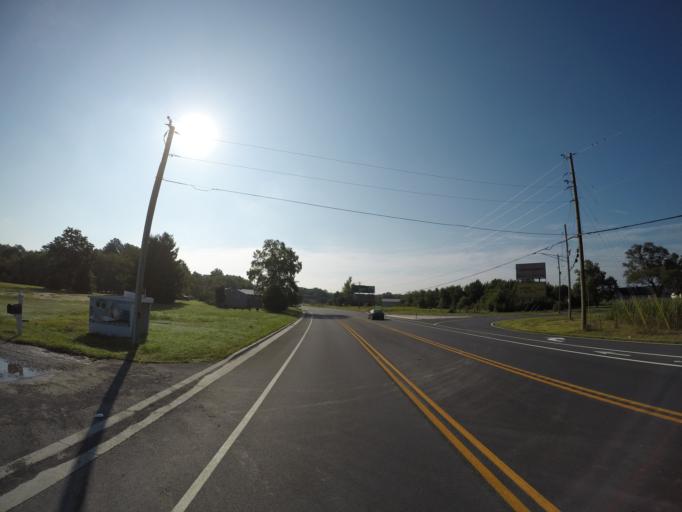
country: US
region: Delaware
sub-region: Sussex County
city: Bridgeville
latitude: 38.7103
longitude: -75.5655
